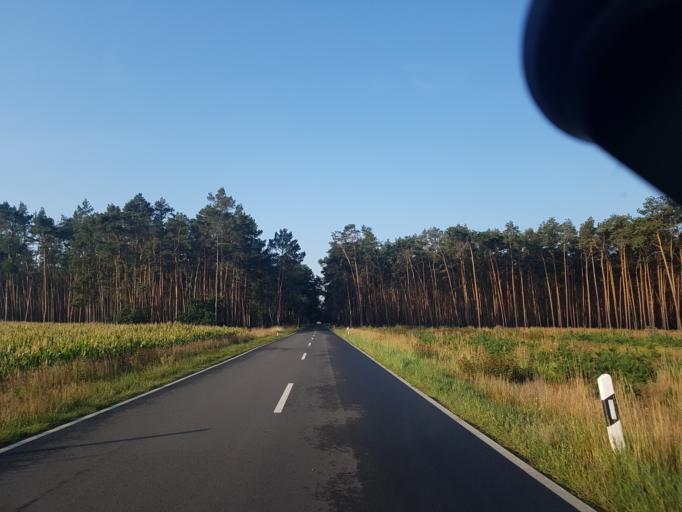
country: DE
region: Saxony-Anhalt
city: Holzdorf
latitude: 51.8076
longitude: 13.1405
